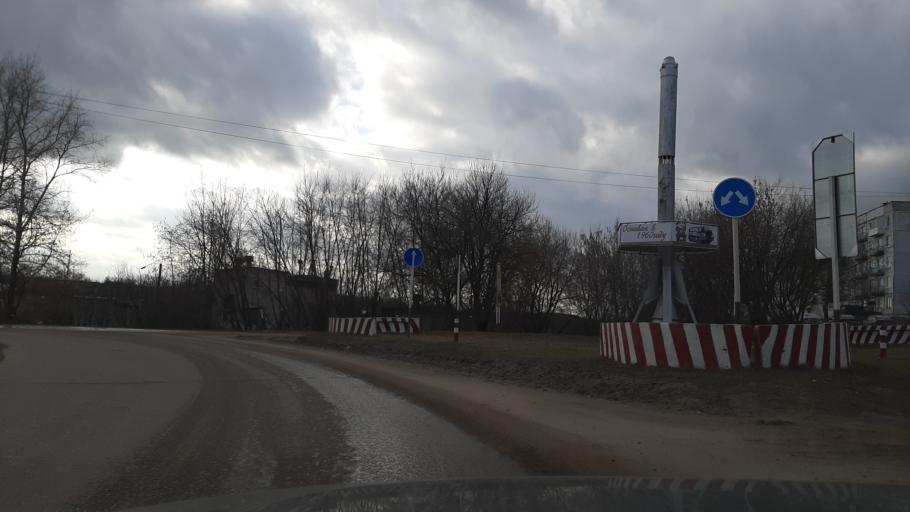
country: RU
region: Ivanovo
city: Teykovo
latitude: 56.8594
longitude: 40.5205
